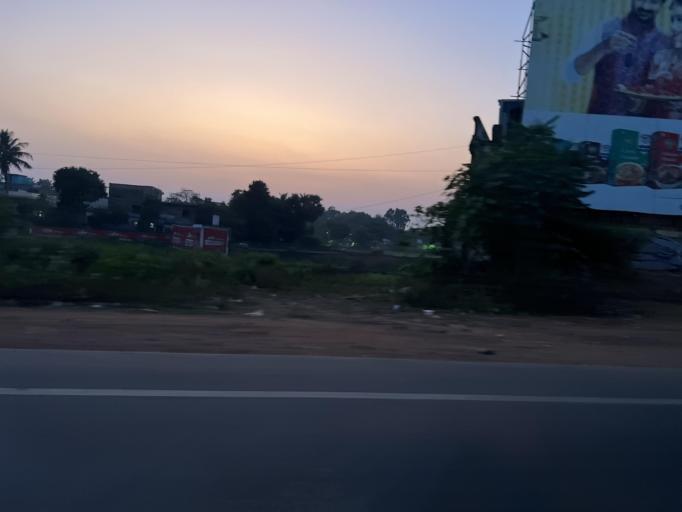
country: IN
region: Odisha
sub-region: Cuttack
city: Cuttack
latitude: 20.4250
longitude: 85.8787
